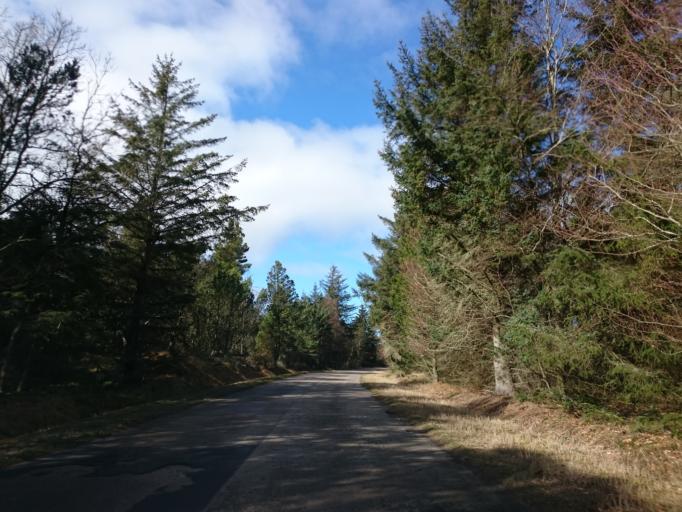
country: DK
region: North Denmark
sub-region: Frederikshavn Kommune
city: Skagen
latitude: 57.6548
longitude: 10.4188
